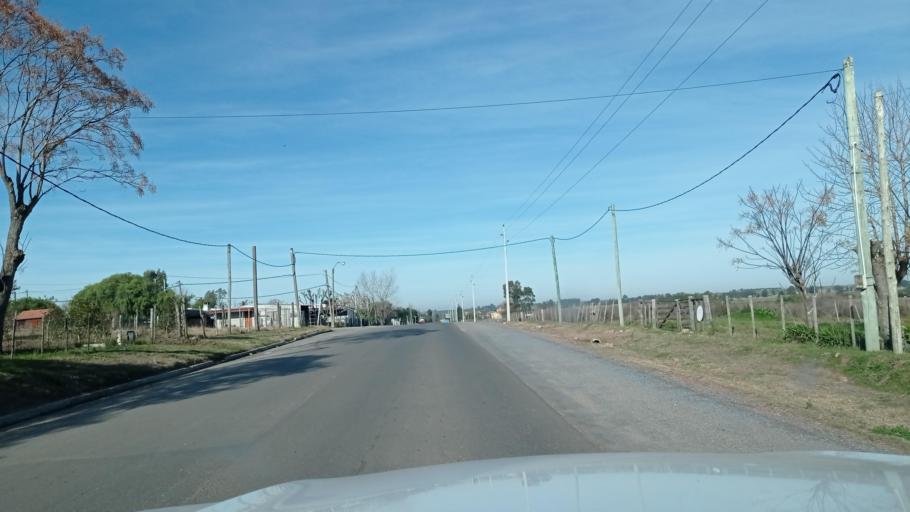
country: UY
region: Florida
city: Florida
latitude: -34.0965
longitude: -56.2405
